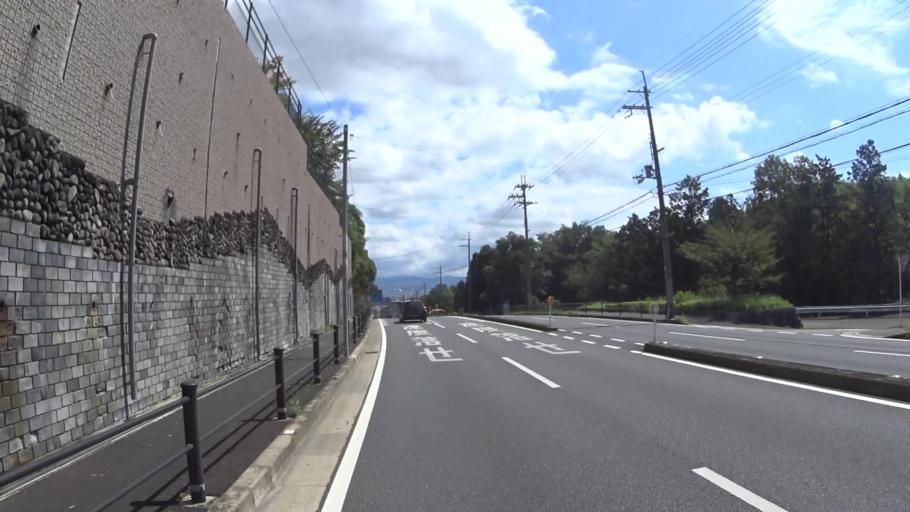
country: JP
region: Kyoto
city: Muko
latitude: 34.9639
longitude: 135.6876
